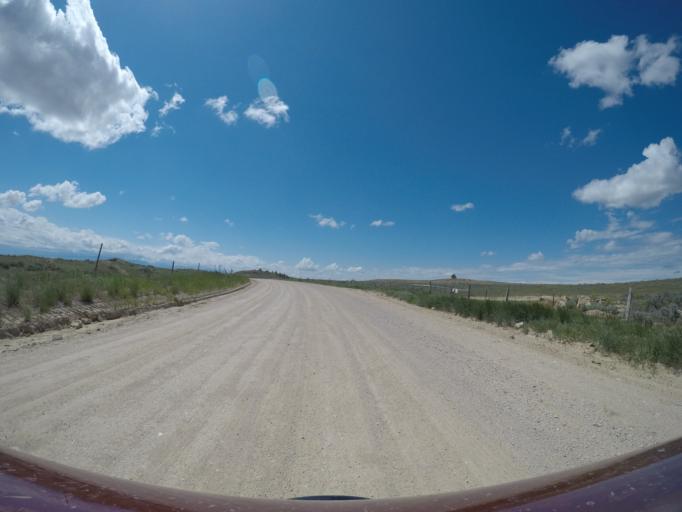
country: US
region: Wyoming
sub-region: Park County
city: Powell
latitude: 45.2065
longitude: -108.7676
